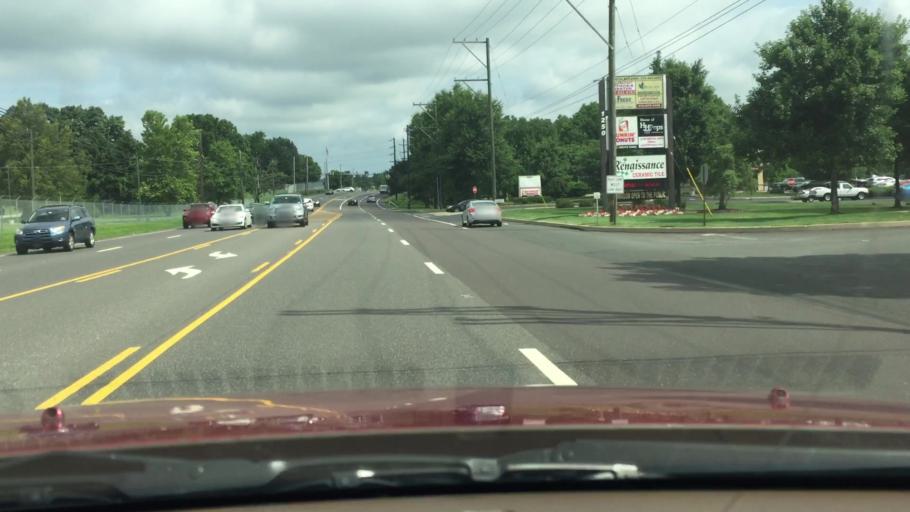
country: US
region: Pennsylvania
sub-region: Montgomery County
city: Horsham
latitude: 40.2033
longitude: -75.1394
